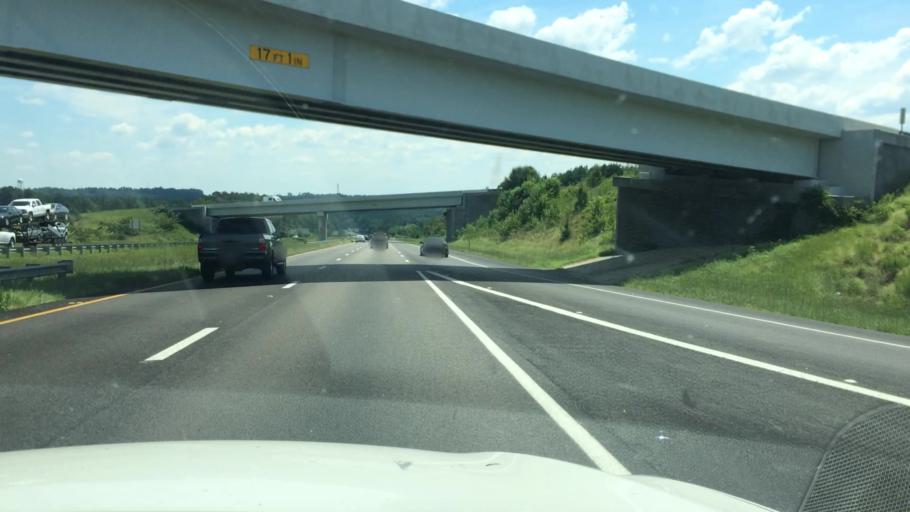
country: US
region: South Carolina
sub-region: Edgefield County
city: Murphys Estates
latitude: 33.5671
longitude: -81.9282
